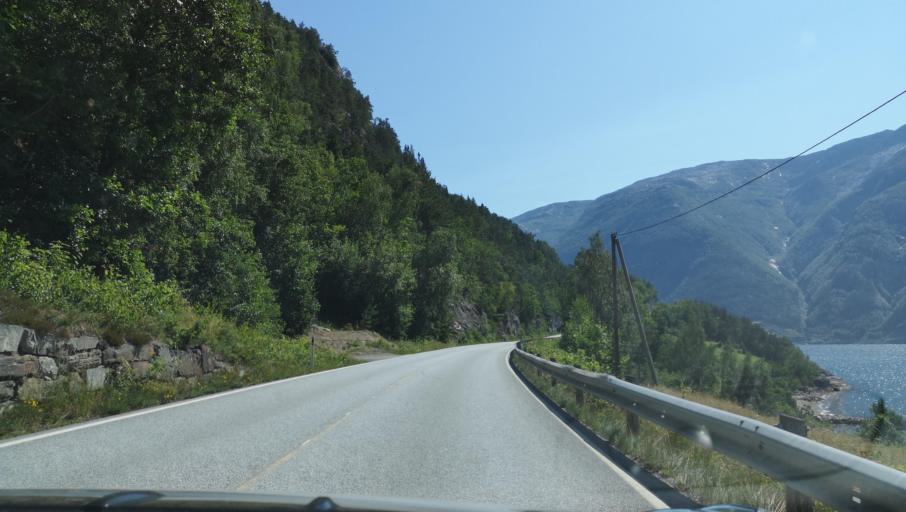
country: NO
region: Hordaland
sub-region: Ulvik
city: Ulvik
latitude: 60.4899
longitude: 6.8673
